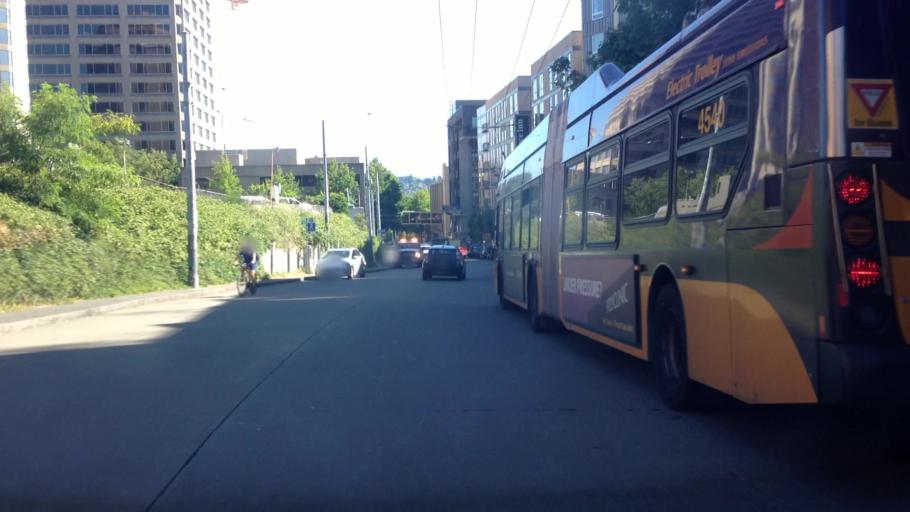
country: US
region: Washington
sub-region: King County
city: Seattle
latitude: 47.6628
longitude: -122.3153
